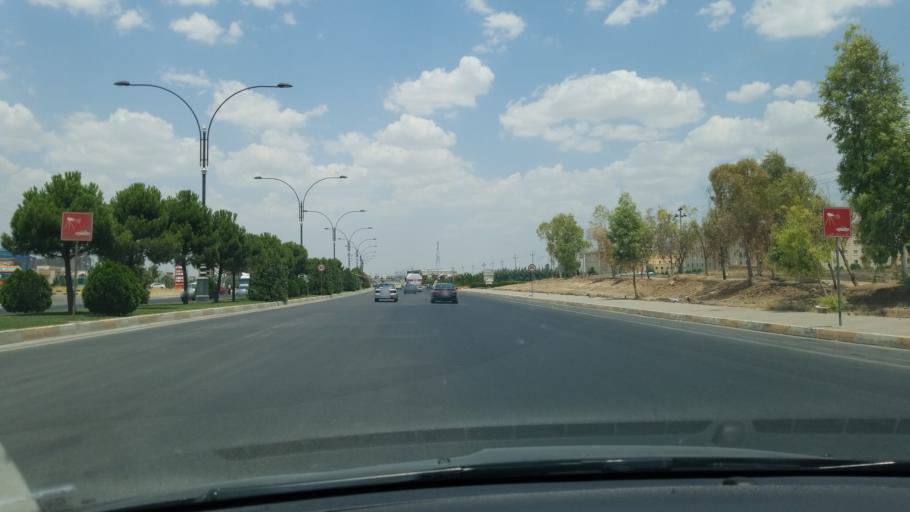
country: IQ
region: Arbil
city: Erbil
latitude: 36.1227
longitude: 44.0241
